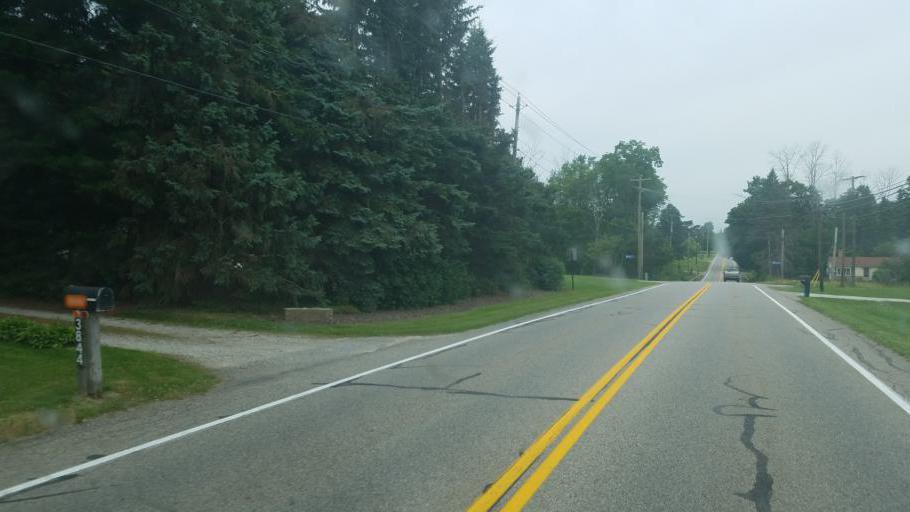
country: US
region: Ohio
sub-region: Portage County
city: Ravenna
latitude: 41.0994
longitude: -81.2541
